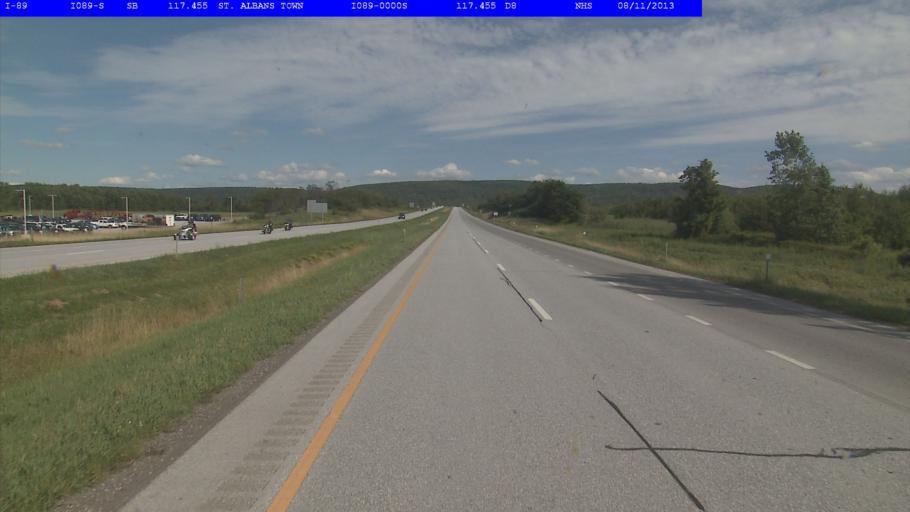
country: US
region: Vermont
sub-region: Franklin County
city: Saint Albans
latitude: 44.8423
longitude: -73.0767
